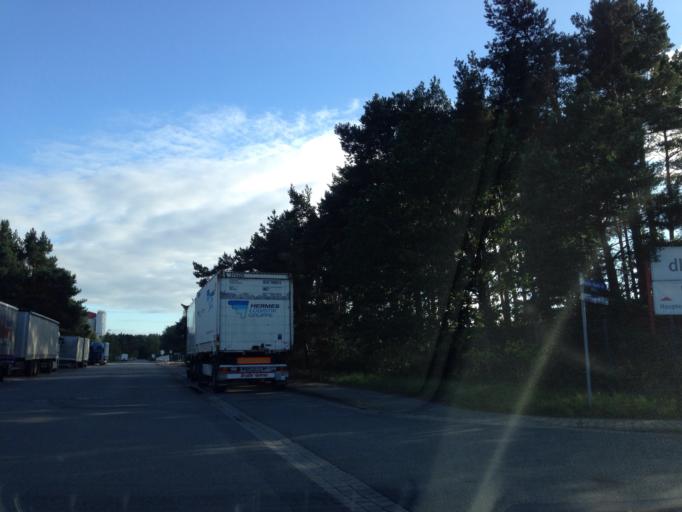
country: DE
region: Lower Saxony
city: Wendisch Evern
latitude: 53.2441
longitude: 10.4780
